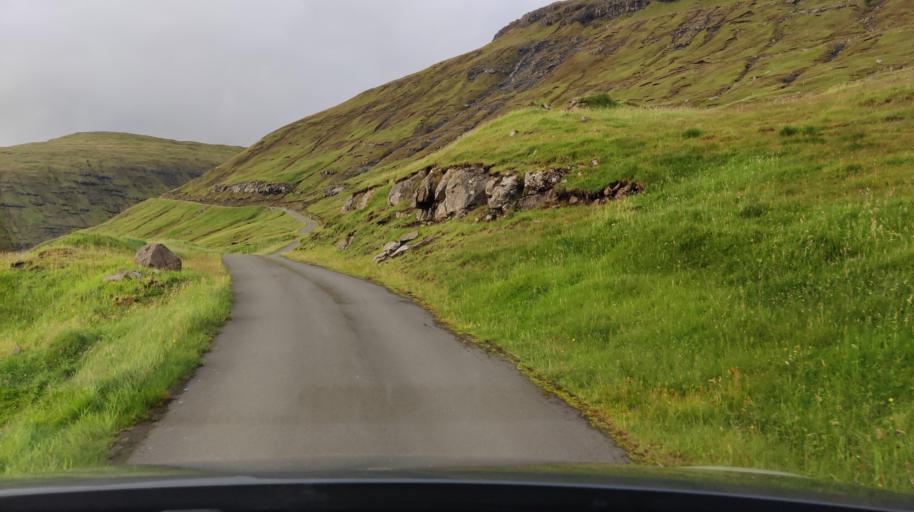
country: FO
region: Streymoy
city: Vestmanna
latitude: 62.1543
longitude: -7.1378
